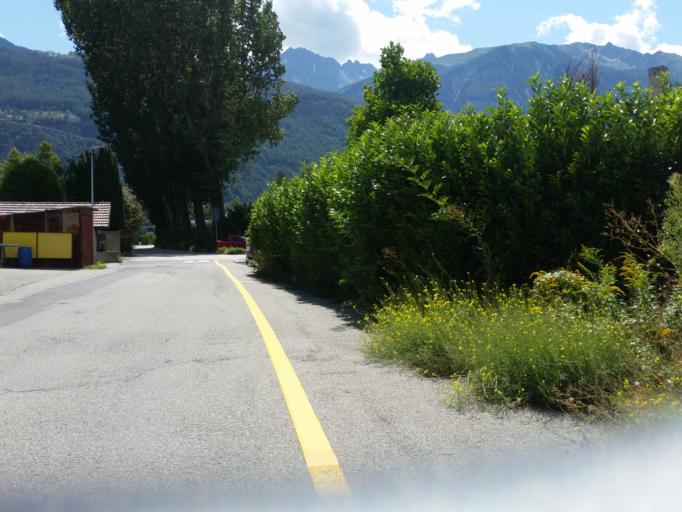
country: CH
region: Valais
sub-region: Martigny District
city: Martigny-Ville
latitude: 46.1089
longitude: 7.0725
